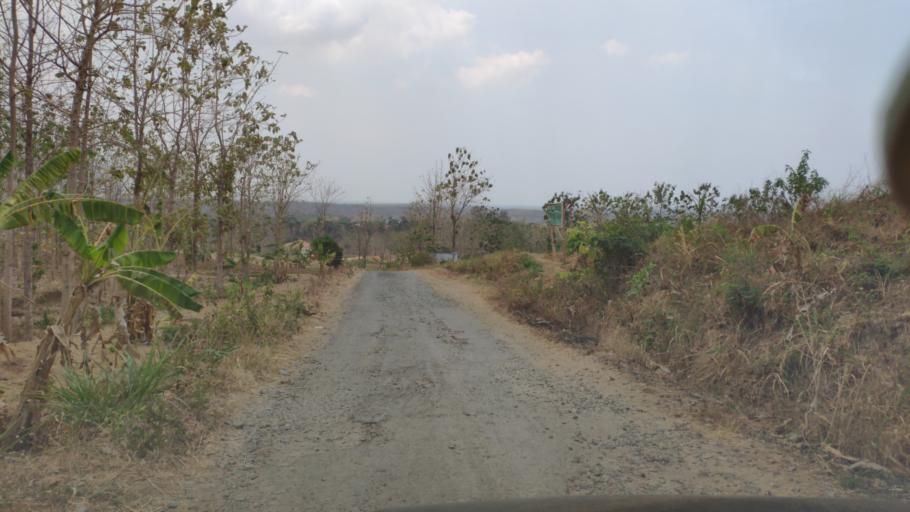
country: ID
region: Central Java
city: Kedungbacin
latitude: -6.8732
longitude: 111.2246
